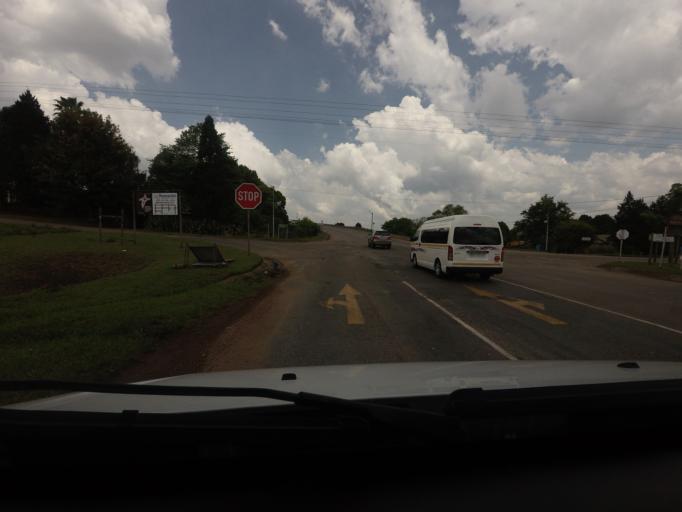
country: ZA
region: Mpumalanga
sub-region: Ehlanzeni District
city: Graksop
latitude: -24.9316
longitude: 30.8377
